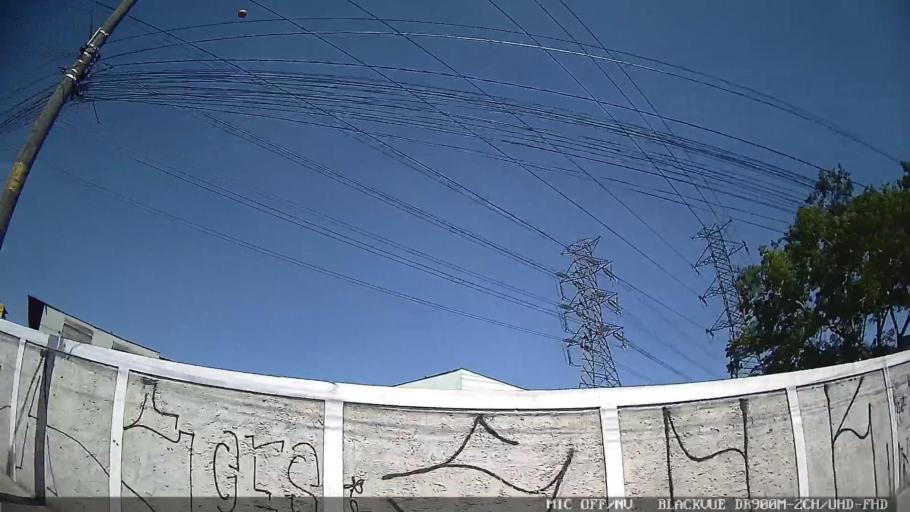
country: BR
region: Sao Paulo
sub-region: Sao Caetano Do Sul
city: Sao Caetano do Sul
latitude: -23.5851
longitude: -46.4924
